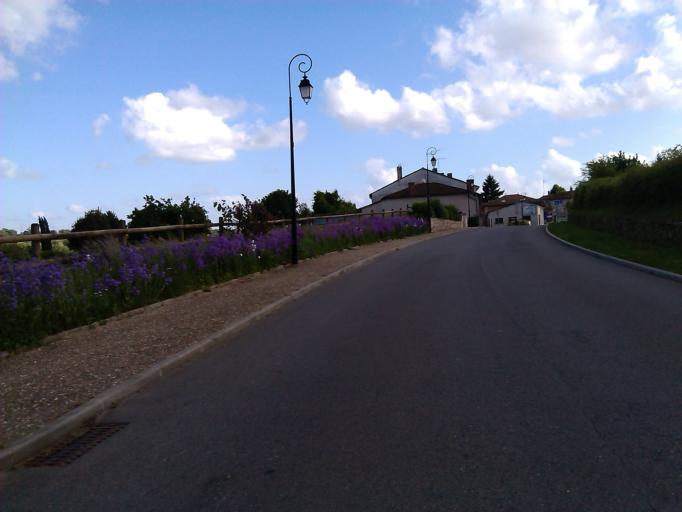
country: FR
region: Poitou-Charentes
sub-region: Departement de la Vienne
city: Availles-Limouzine
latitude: 46.2323
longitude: 0.6767
